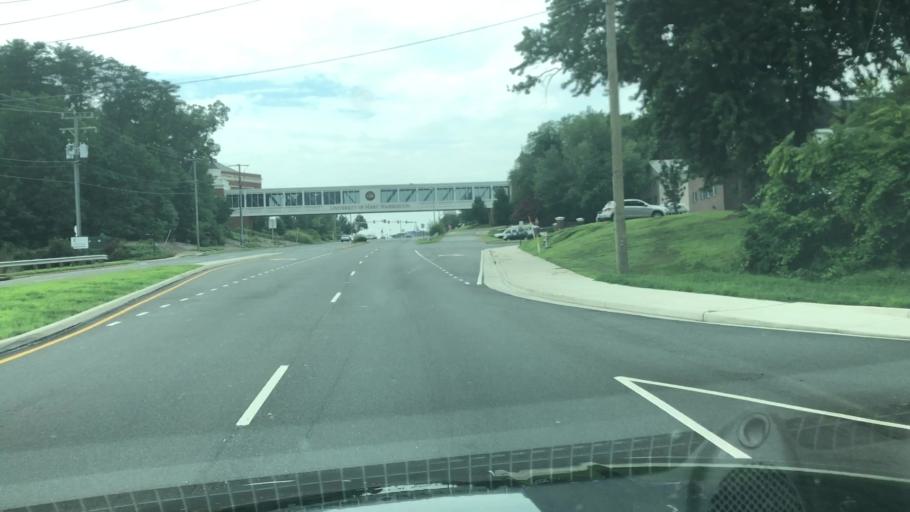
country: US
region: Virginia
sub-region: Stafford County
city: Falmouth
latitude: 38.3093
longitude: -77.4781
